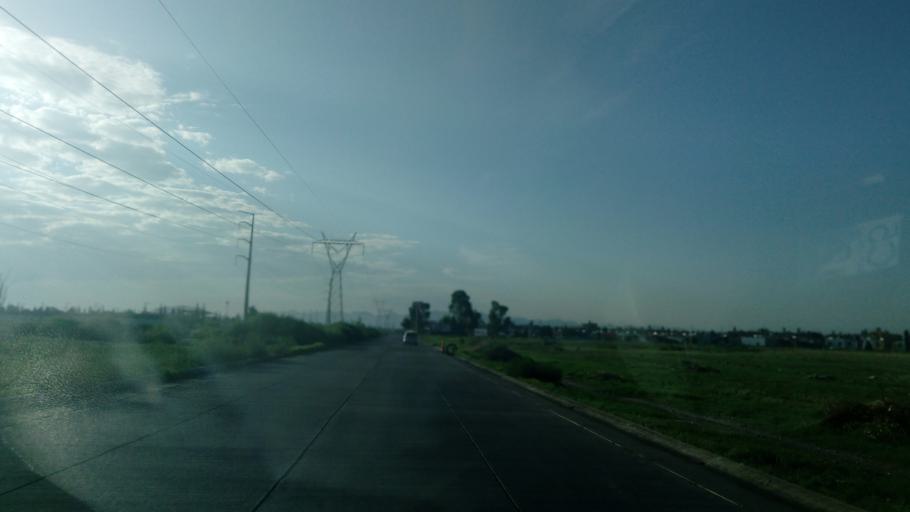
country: MX
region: Durango
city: Victoria de Durango
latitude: 24.0762
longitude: -104.5902
